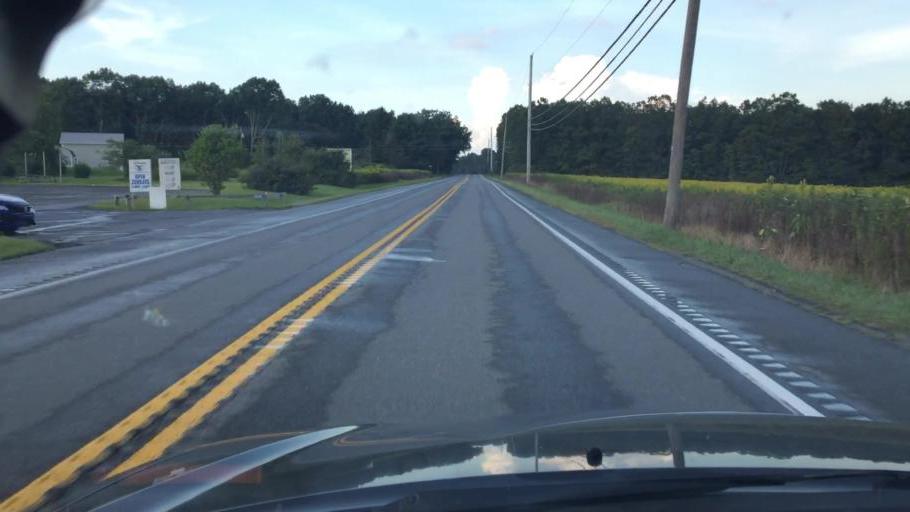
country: US
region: Pennsylvania
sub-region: Carbon County
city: Jim Thorpe
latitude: 40.9112
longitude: -75.6738
